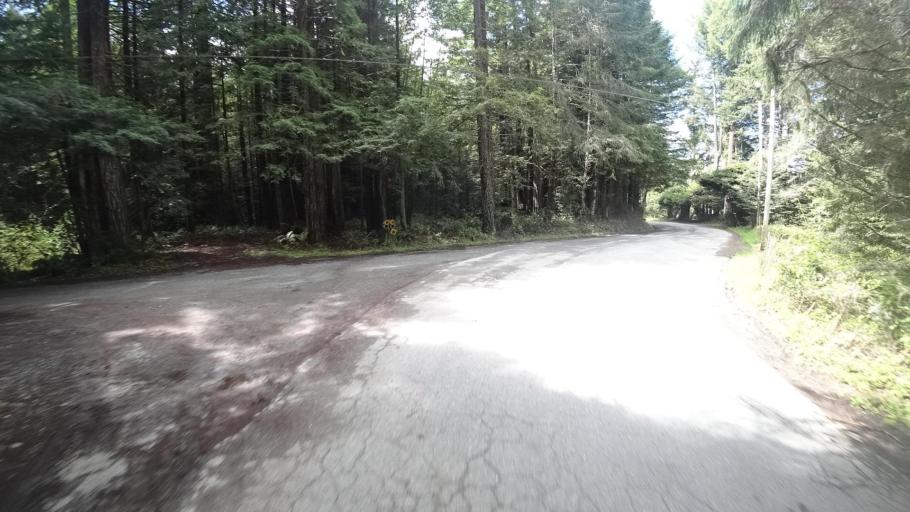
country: US
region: California
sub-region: Humboldt County
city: Blue Lake
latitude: 40.9004
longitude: -123.9882
